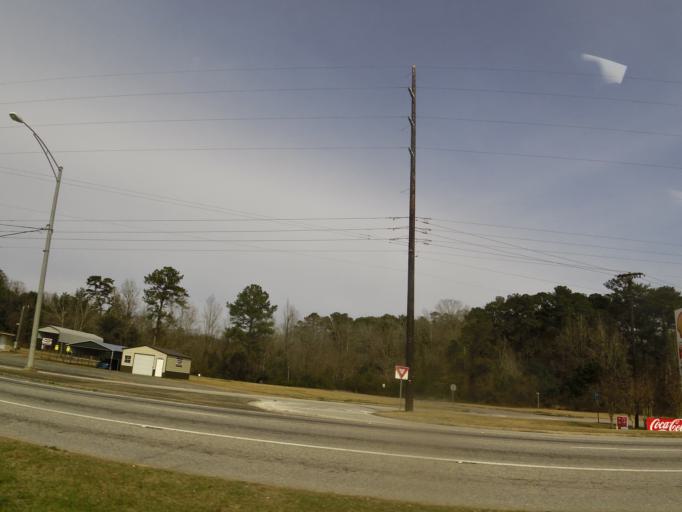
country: US
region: Alabama
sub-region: Dale County
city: Ozark
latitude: 31.4395
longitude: -85.6432
